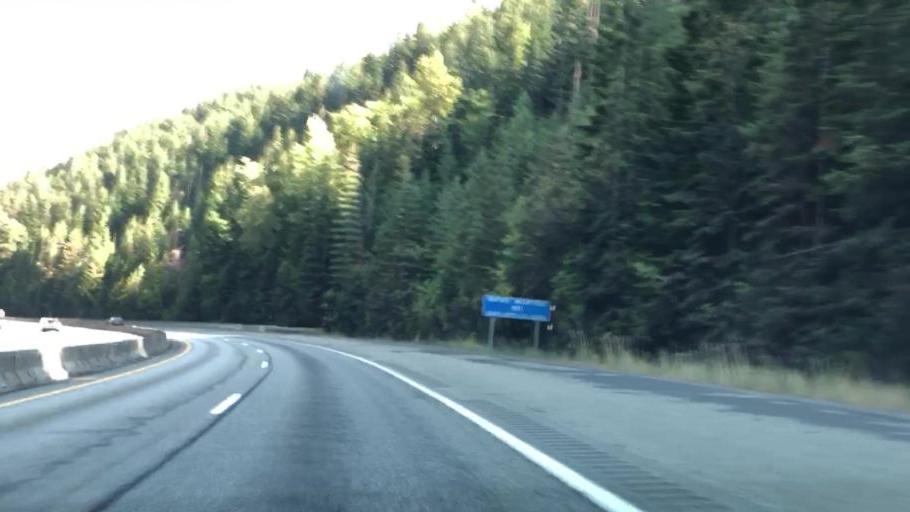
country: US
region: Idaho
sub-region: Shoshone County
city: Pinehurst
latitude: 47.5913
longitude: -116.4915
